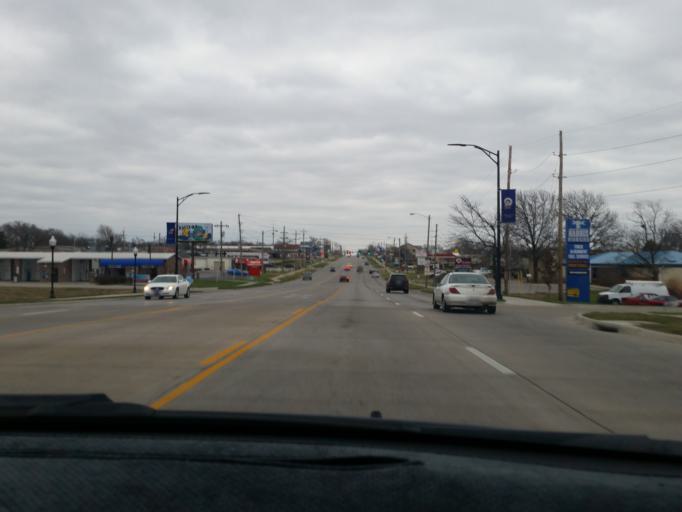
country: US
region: Kansas
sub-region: Douglas County
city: Lawrence
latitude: 38.9427
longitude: -95.2267
